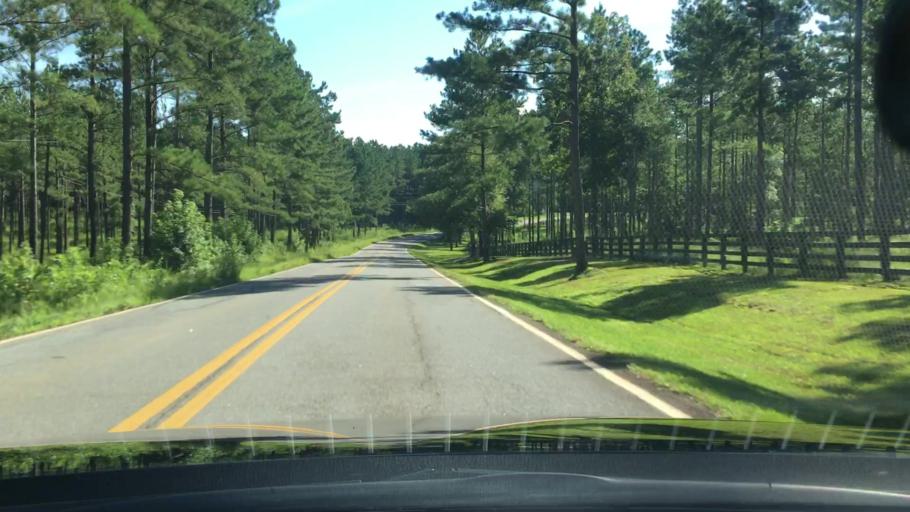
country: US
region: Georgia
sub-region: Putnam County
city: Jefferson
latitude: 33.4350
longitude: -83.3689
